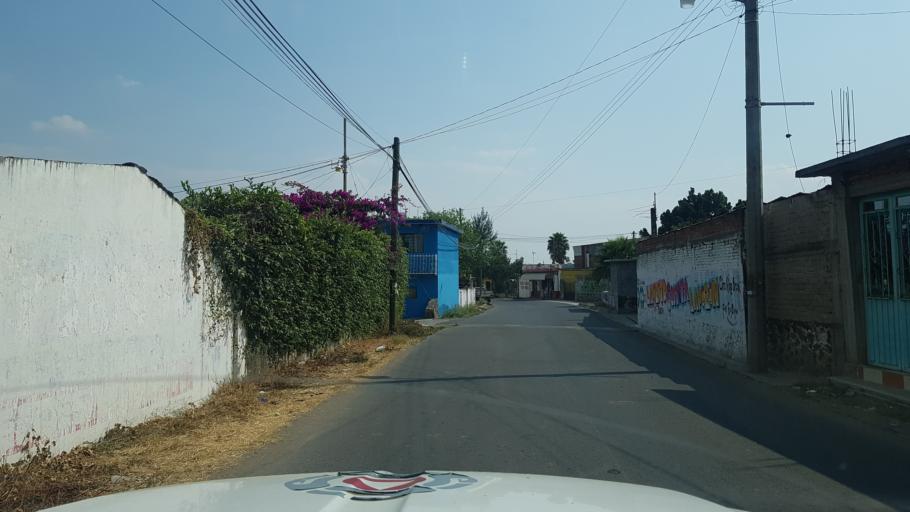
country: MX
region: Morelos
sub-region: Yecapixtla
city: Yecapixtla
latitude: 18.8907
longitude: -98.8635
